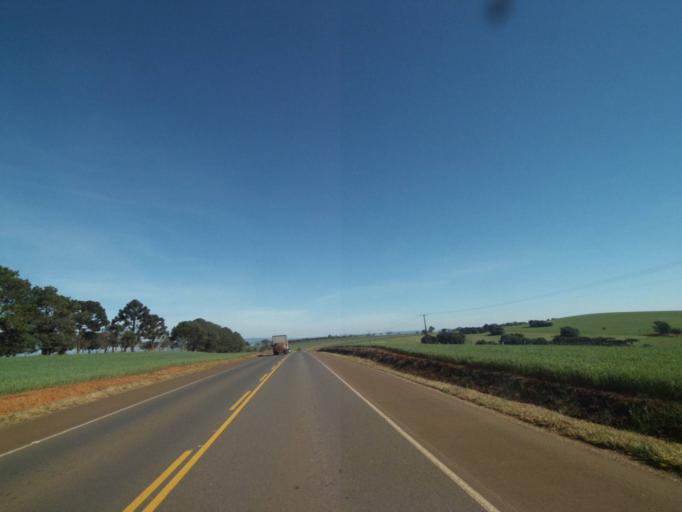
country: BR
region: Parana
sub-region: Tibagi
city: Tibagi
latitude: -24.4190
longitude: -50.3701
